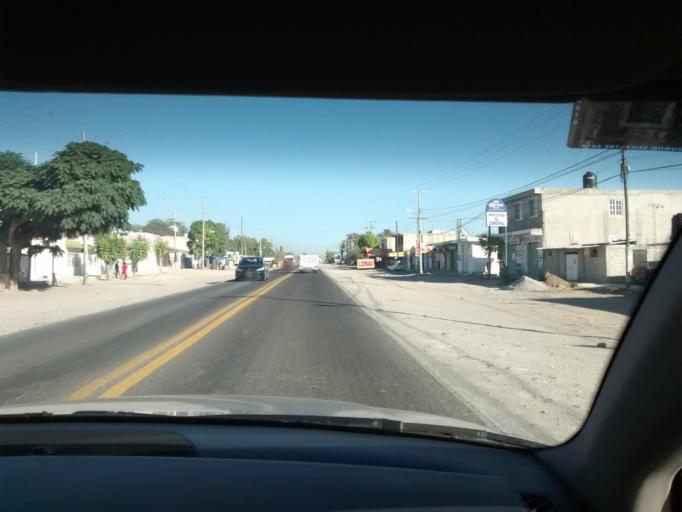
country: MX
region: Puebla
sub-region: Santiago Miahuatlan
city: San Jose Monte Chiquito
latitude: 18.4906
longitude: -97.4617
